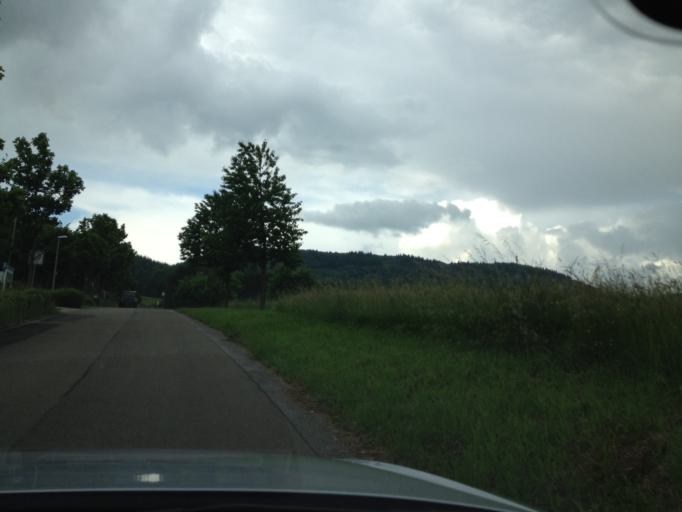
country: DE
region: Saarland
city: Freisen
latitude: 49.5330
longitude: 7.2606
